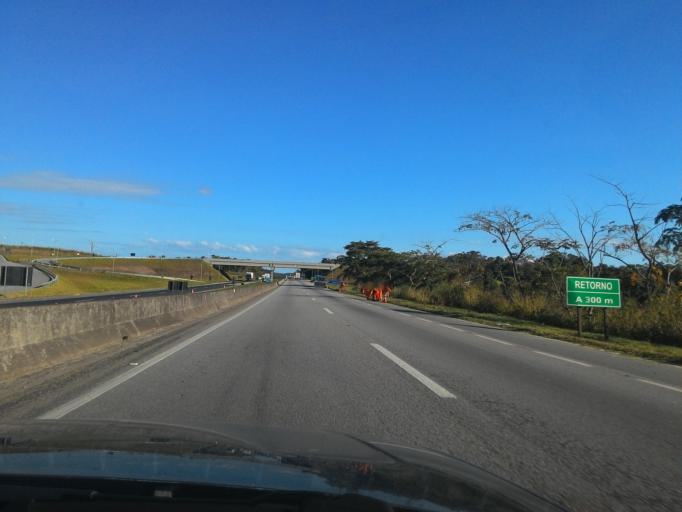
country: BR
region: Sao Paulo
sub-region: Registro
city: Registro
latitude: -24.5365
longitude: -47.8590
